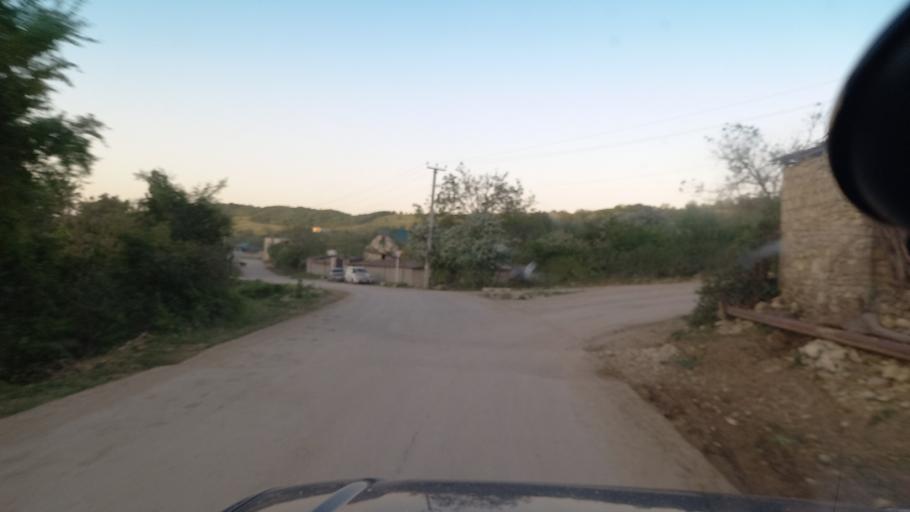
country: RU
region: Dagestan
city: Khuchni
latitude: 42.0315
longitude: 47.9706
